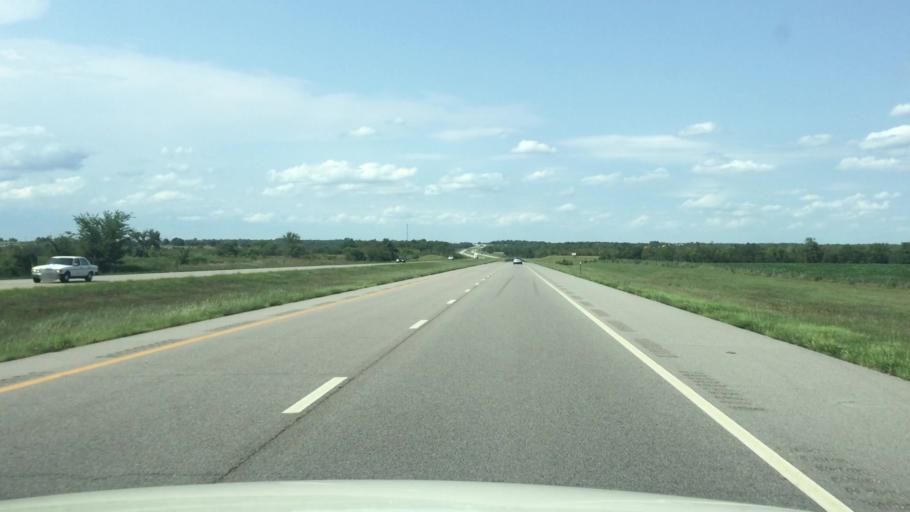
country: US
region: Kansas
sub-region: Linn County
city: La Cygne
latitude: 38.4405
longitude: -94.6864
